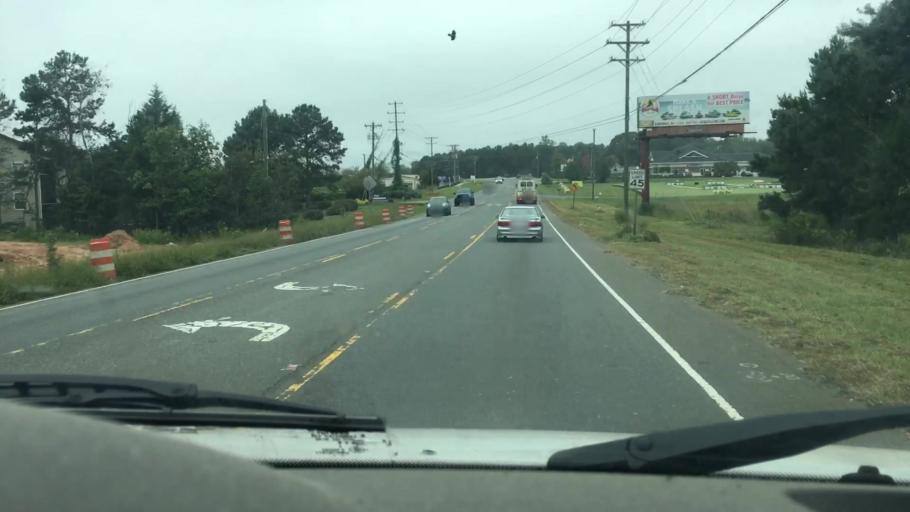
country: US
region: North Carolina
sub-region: Catawba County
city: Lake Norman of Catawba
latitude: 35.6034
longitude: -80.9011
